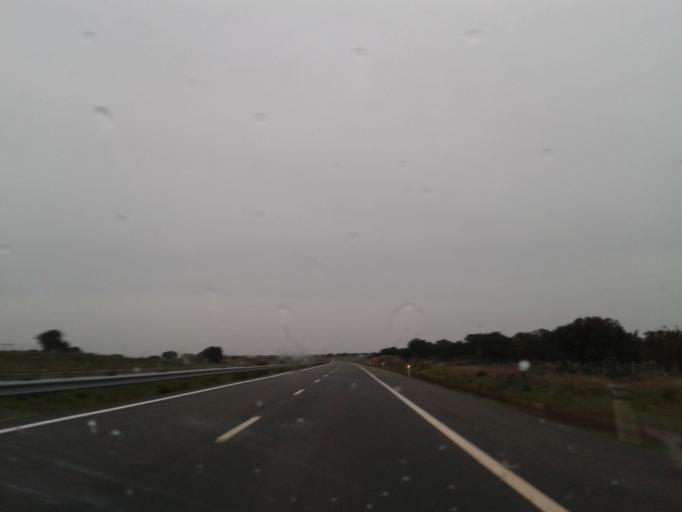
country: PT
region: Beja
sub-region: Aljustrel
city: Aljustrel
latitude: 38.0158
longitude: -8.2804
